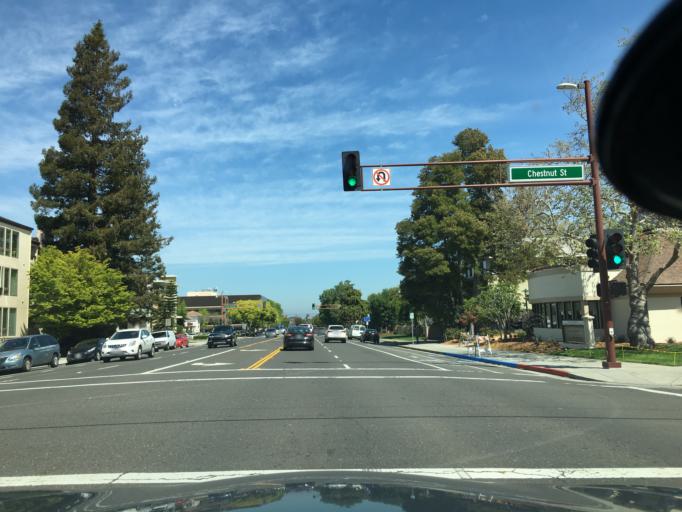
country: US
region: California
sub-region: San Mateo County
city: San Carlos
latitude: 37.5043
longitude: -122.2642
